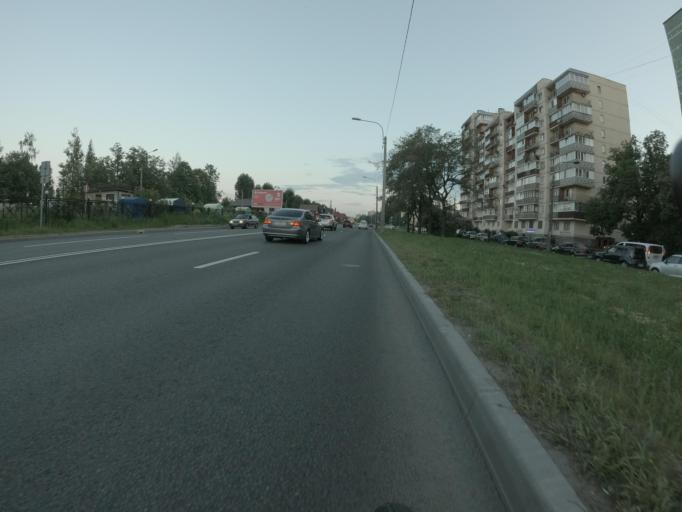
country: RU
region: St.-Petersburg
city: Dachnoye
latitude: 59.8446
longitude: 30.2787
